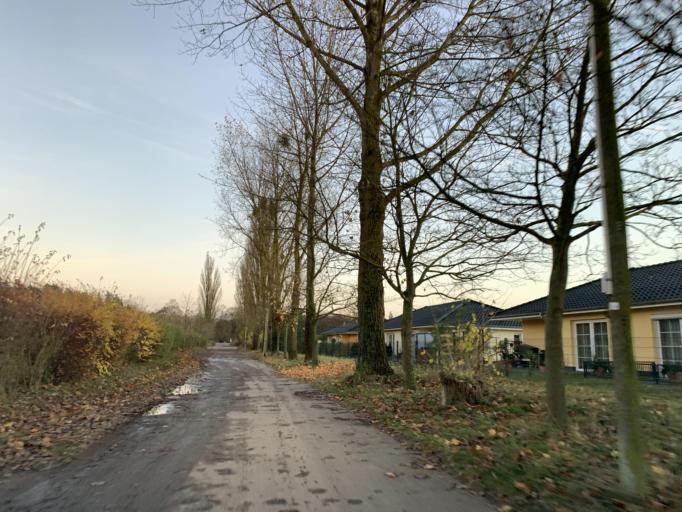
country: DE
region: Mecklenburg-Vorpommern
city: Loitz
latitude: 53.3281
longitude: 13.4380
